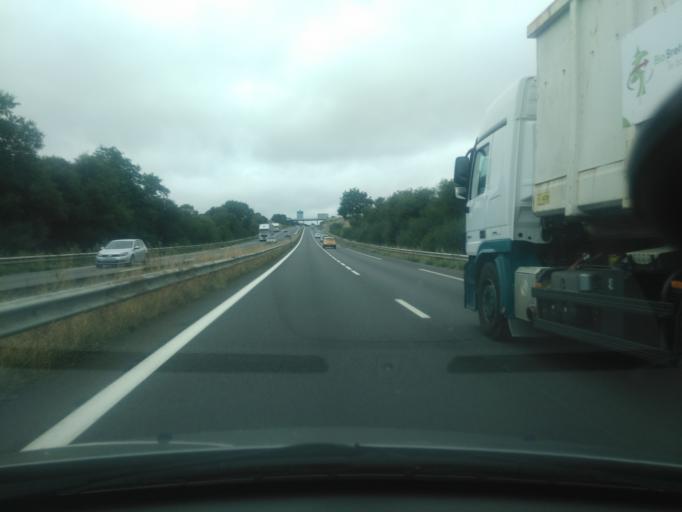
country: FR
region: Brittany
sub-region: Departement des Cotes-d'Armor
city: Lamballe
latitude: 48.4585
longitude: -2.5248
